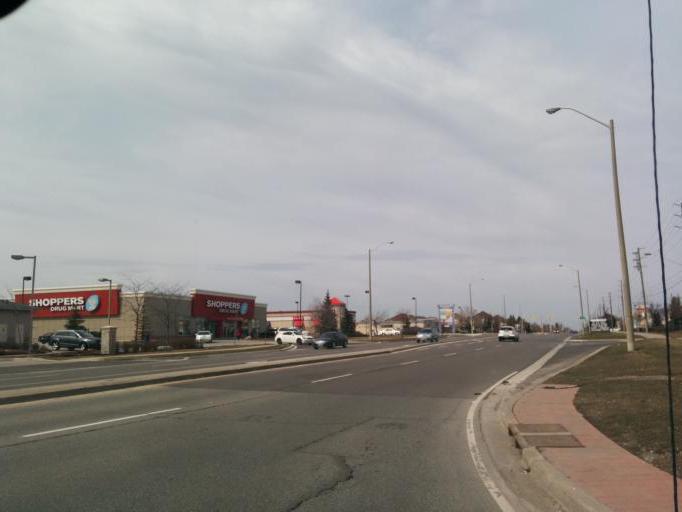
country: CA
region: Ontario
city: Brampton
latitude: 43.6963
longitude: -79.7978
